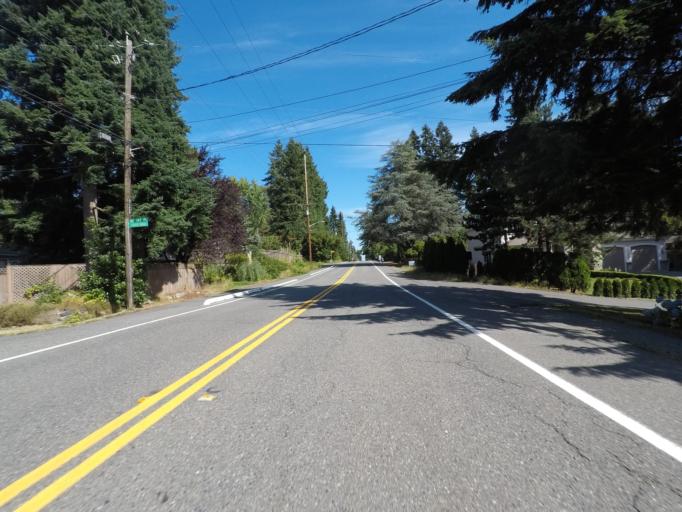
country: US
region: Washington
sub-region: King County
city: Inglewood-Finn Hill
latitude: 47.7350
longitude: -122.2290
